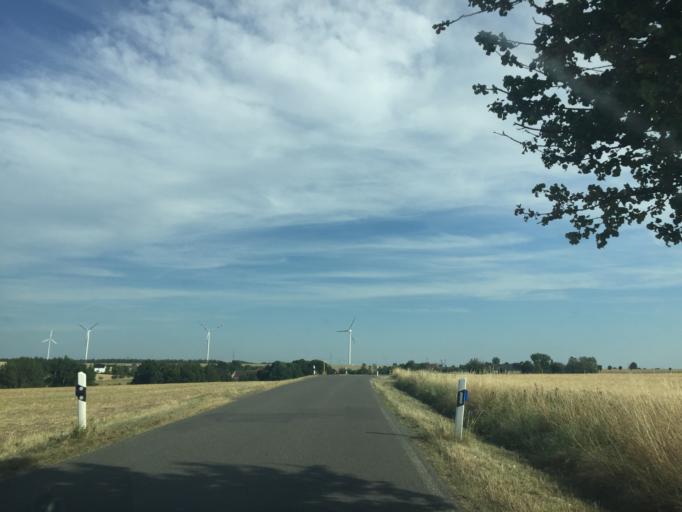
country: DE
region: Thuringia
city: Schmolln
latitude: 50.8818
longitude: 12.3697
